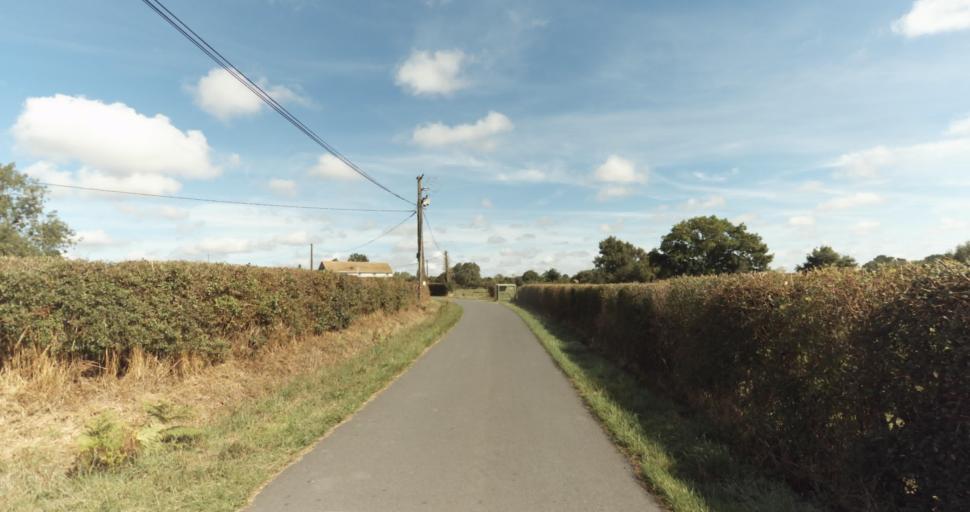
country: FR
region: Lower Normandy
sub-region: Departement du Calvados
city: Orbec
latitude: 48.9569
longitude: 0.3773
